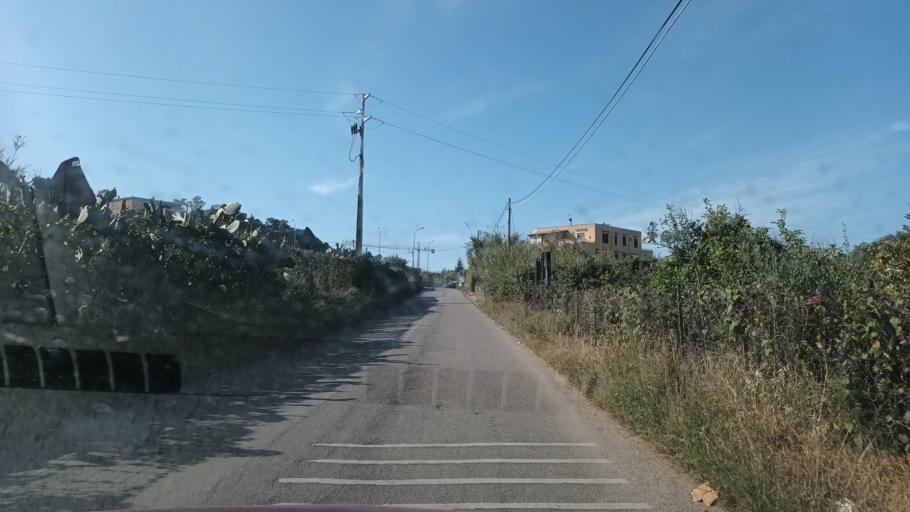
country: IT
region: Sicily
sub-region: Palermo
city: Bagheria
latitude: 38.0657
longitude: 13.5185
